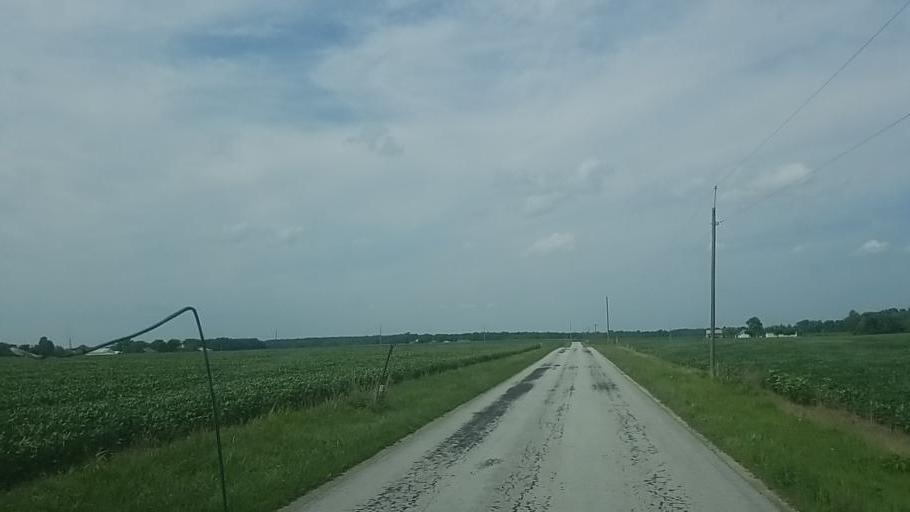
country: US
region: Ohio
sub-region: Hardin County
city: Forest
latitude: 40.7771
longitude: -83.5572
